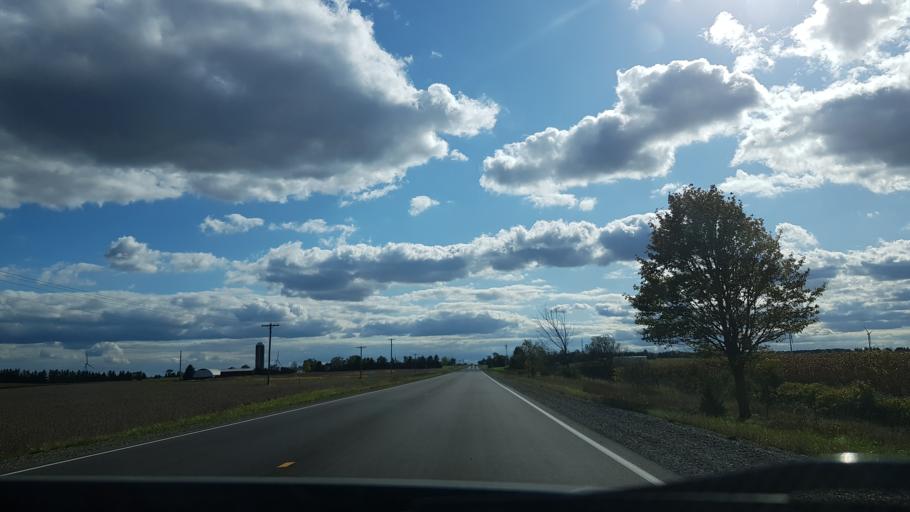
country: CA
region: Ontario
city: South Huron
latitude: 43.1188
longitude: -81.6717
